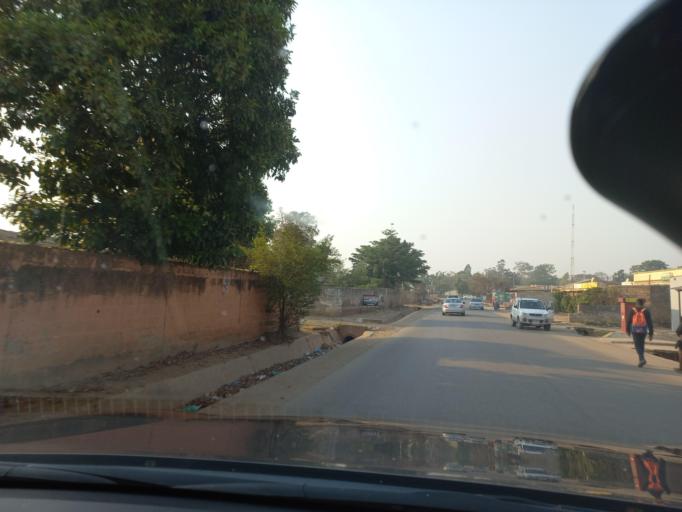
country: ZM
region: Lusaka
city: Lusaka
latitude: -15.4066
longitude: 28.3455
